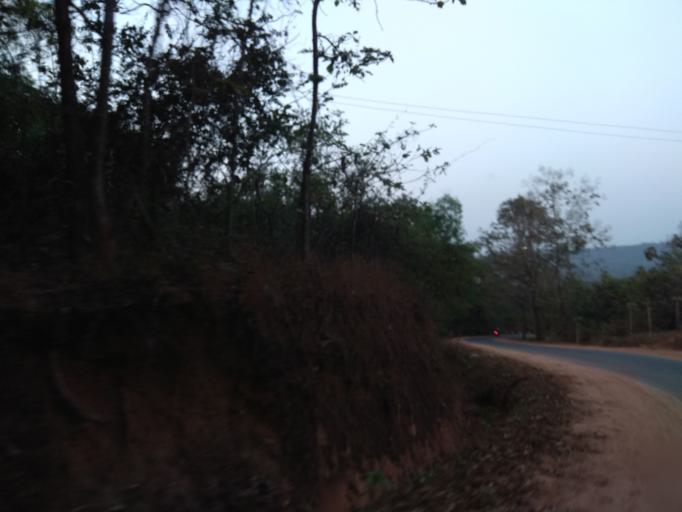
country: IN
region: Karnataka
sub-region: Dakshina Kannada
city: Mangalore
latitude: 12.9282
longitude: 74.8726
